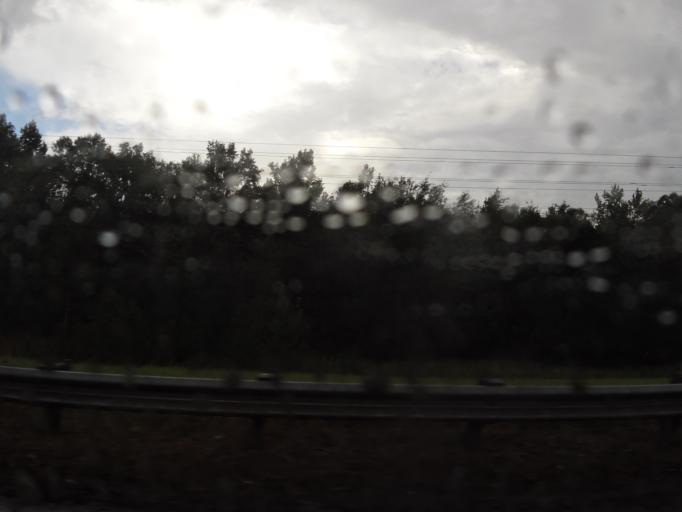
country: US
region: Florida
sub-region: Nassau County
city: Callahan
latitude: 30.5251
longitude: -82.0153
